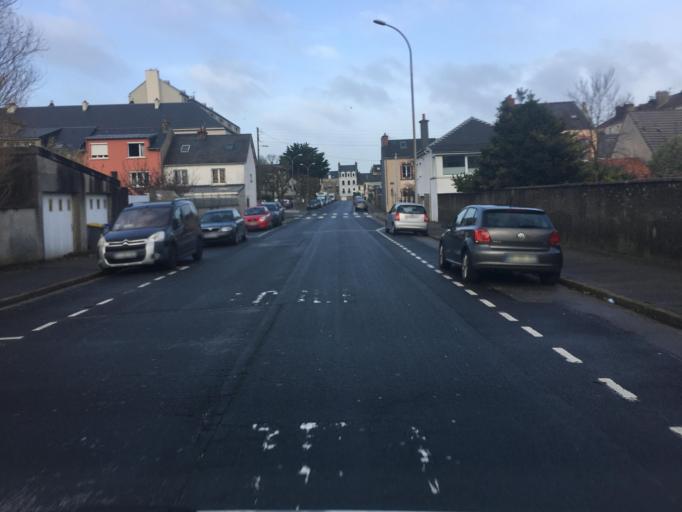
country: FR
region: Lower Normandy
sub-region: Departement de la Manche
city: Cherbourg-Octeville
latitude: 49.6370
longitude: -1.6053
